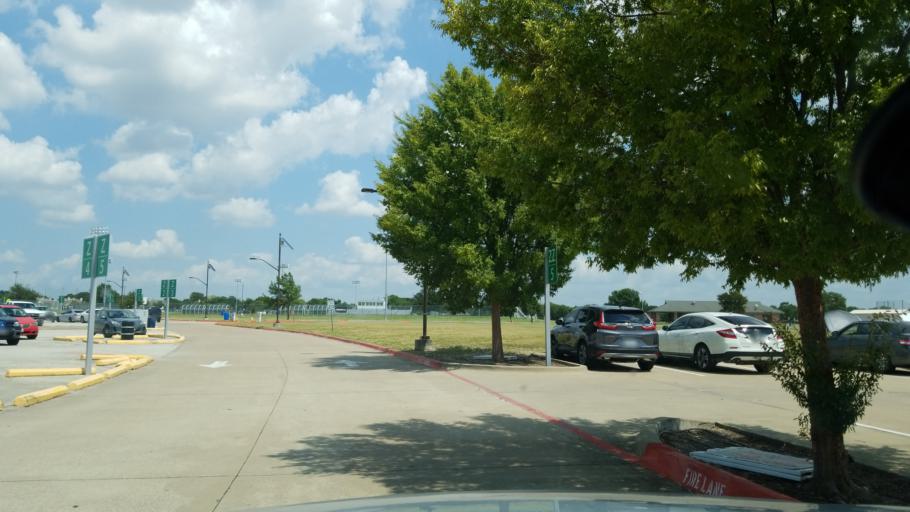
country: US
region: Texas
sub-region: Dallas County
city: Richardson
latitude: 32.9198
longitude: -96.7274
